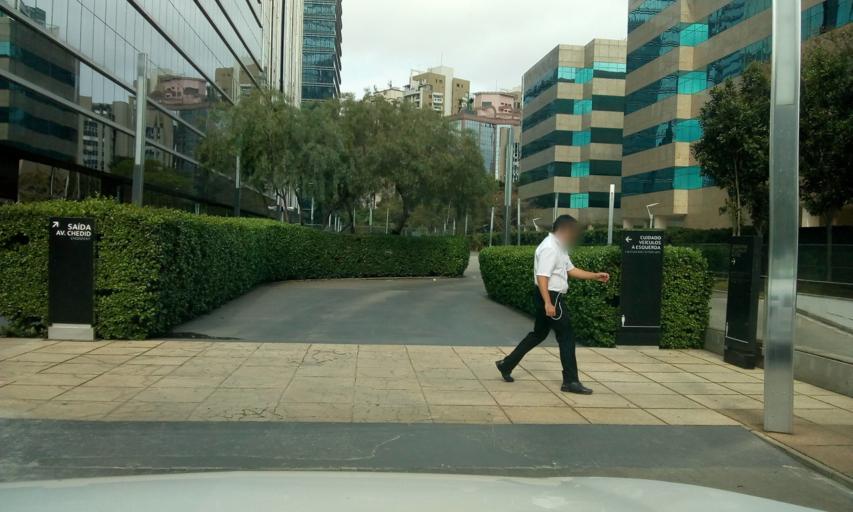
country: BR
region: Sao Paulo
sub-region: Sao Paulo
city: Sao Paulo
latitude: -23.5919
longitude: -46.6905
